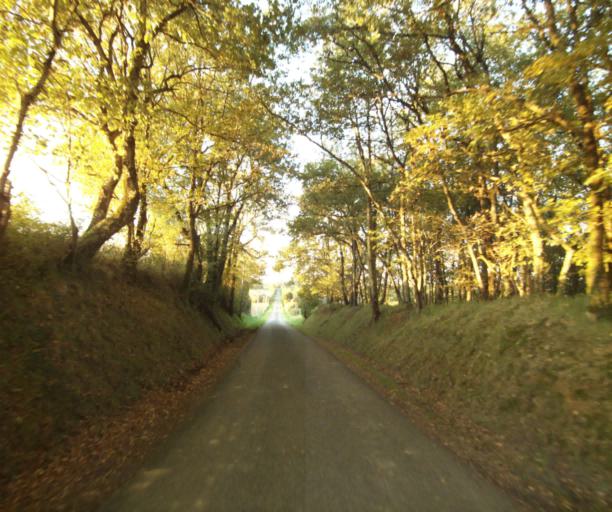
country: FR
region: Midi-Pyrenees
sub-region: Departement du Gers
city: Vic-Fezensac
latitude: 43.7543
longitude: 0.1973
